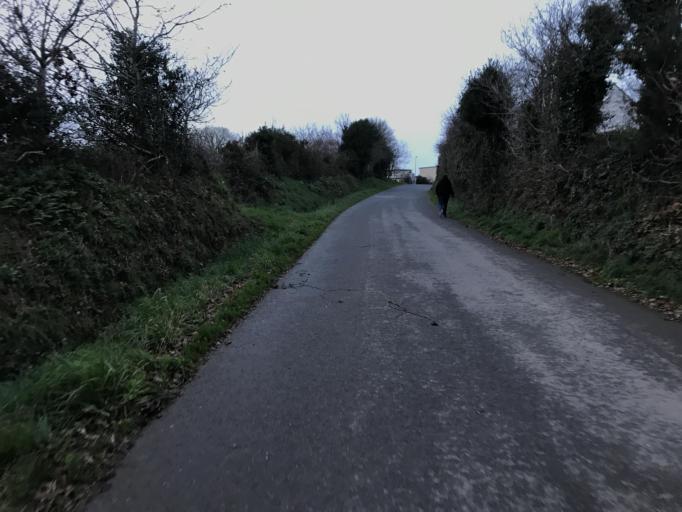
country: FR
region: Brittany
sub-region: Departement du Finistere
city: Loperhet
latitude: 48.3704
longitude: -4.3174
